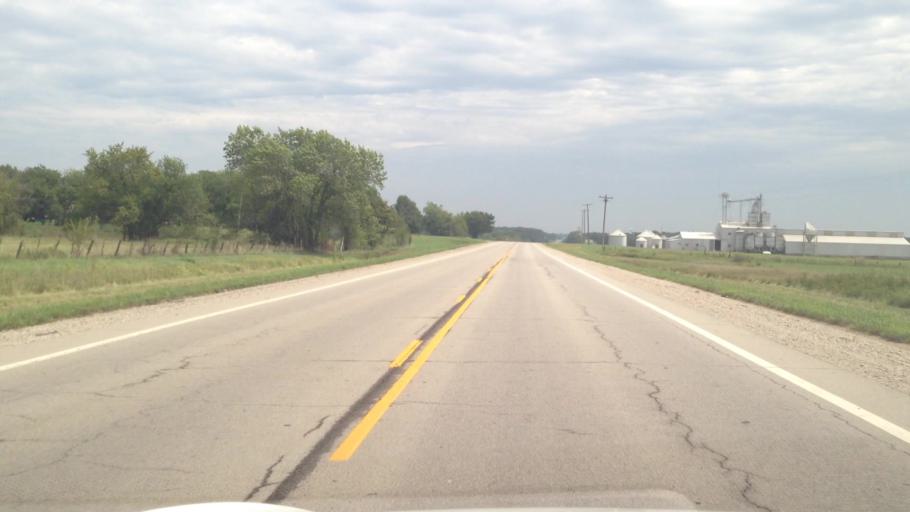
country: US
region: Kansas
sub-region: Crawford County
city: Girard
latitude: 37.5144
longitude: -94.9172
